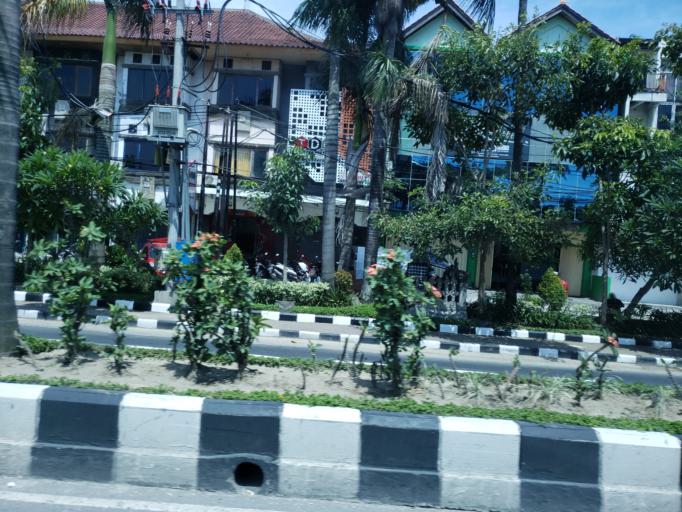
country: ID
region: Bali
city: Kelanabian
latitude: -8.7413
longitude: 115.1808
